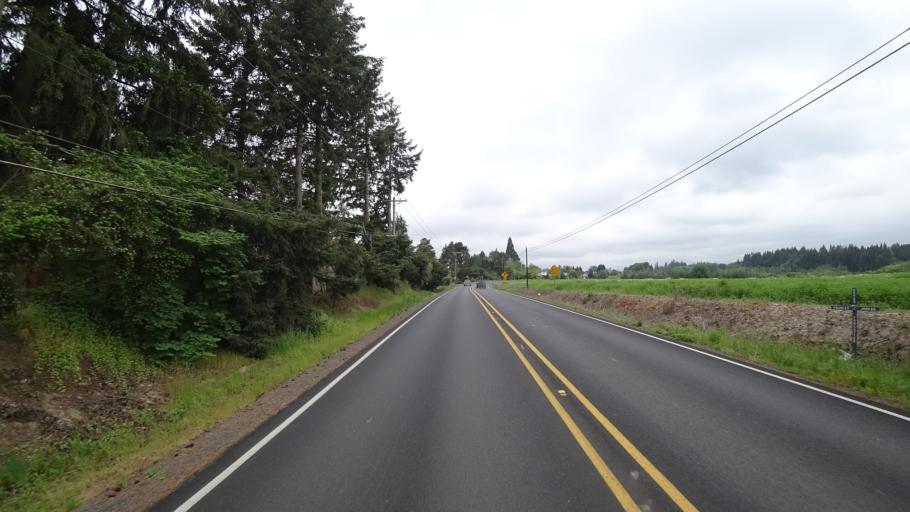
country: US
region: Oregon
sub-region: Washington County
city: Rockcreek
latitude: 45.5600
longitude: -122.8816
